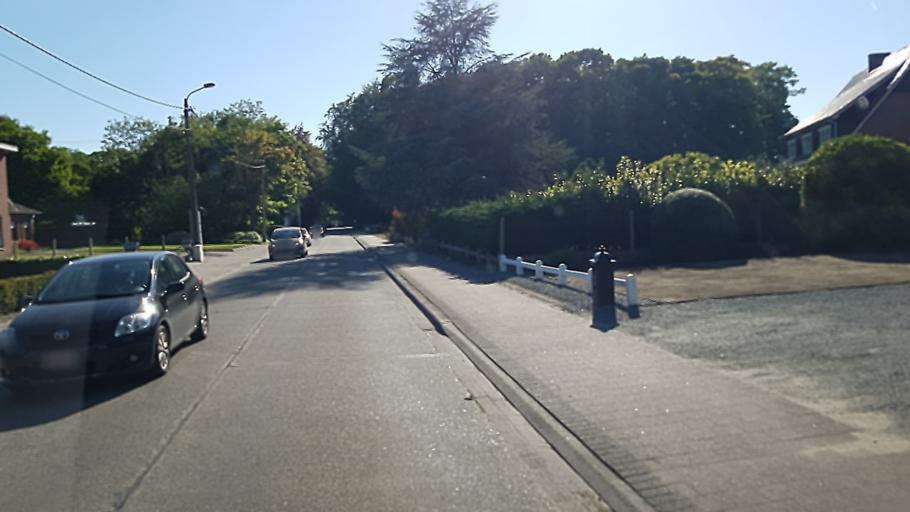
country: BE
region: Flanders
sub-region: Provincie Antwerpen
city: Heist-op-den-Berg
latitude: 51.0999
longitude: 4.7152
